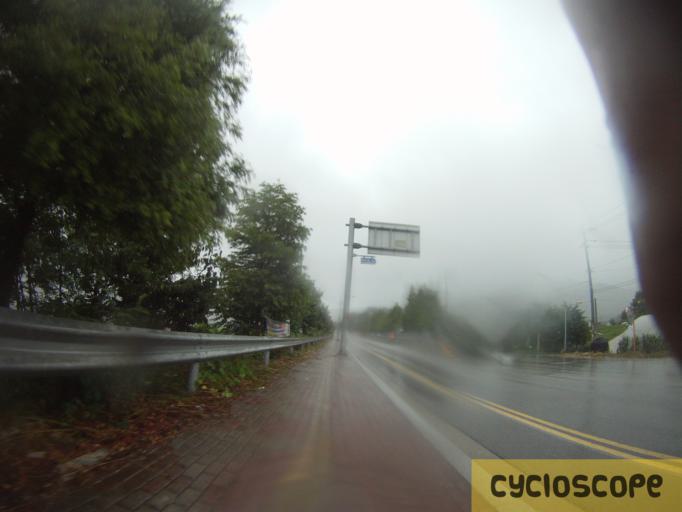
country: KR
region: Chungcheongnam-do
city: Asan
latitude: 36.9603
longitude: 126.8557
